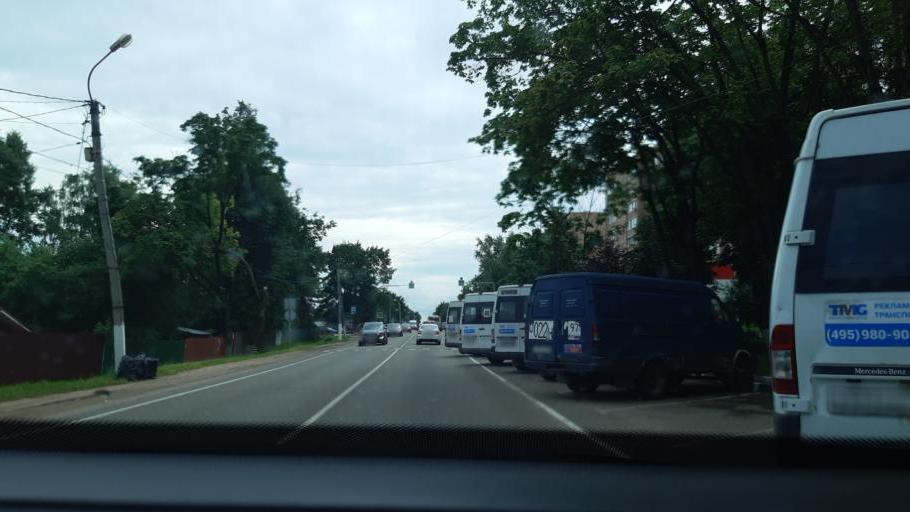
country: RU
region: Moskovskaya
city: Bol'shiye Vyazemy
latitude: 55.6215
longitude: 36.9845
